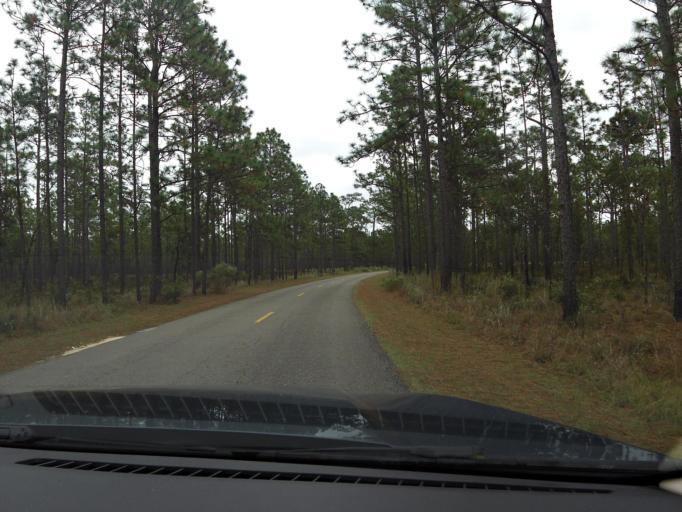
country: US
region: Florida
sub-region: Clay County
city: Keystone Heights
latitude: 29.8472
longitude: -81.9579
